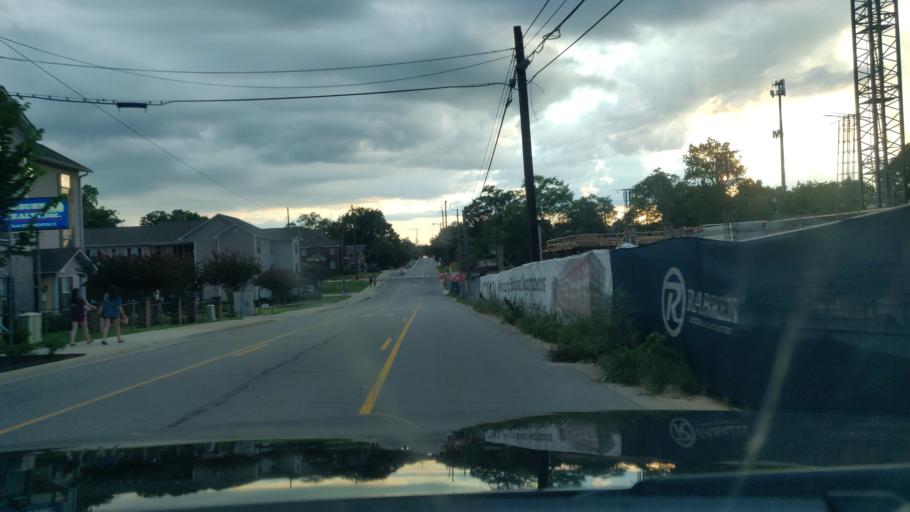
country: US
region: Alabama
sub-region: Lee County
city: Auburn
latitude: 32.6091
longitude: -85.4838
